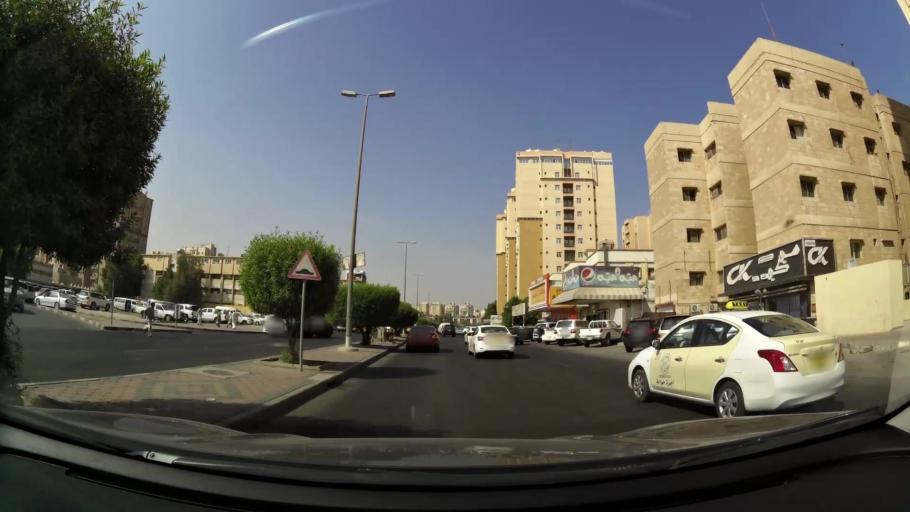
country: KW
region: Al Ahmadi
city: Al Fahahil
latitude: 29.0862
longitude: 48.1317
